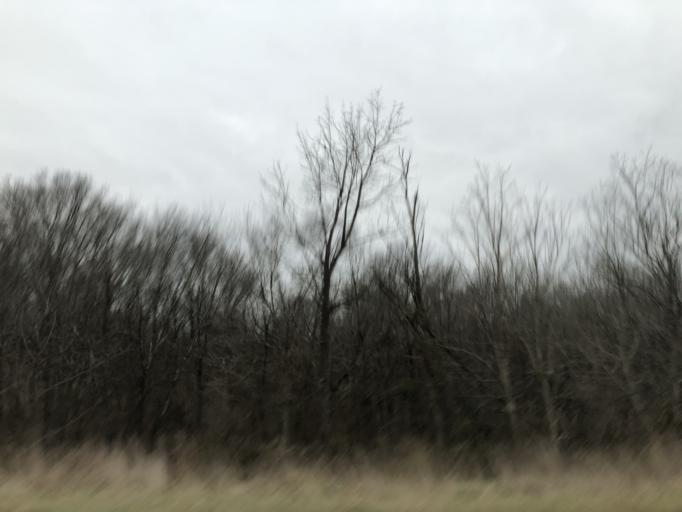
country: US
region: Illinois
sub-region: Johnson County
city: Vienna
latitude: 37.4553
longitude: -88.8889
